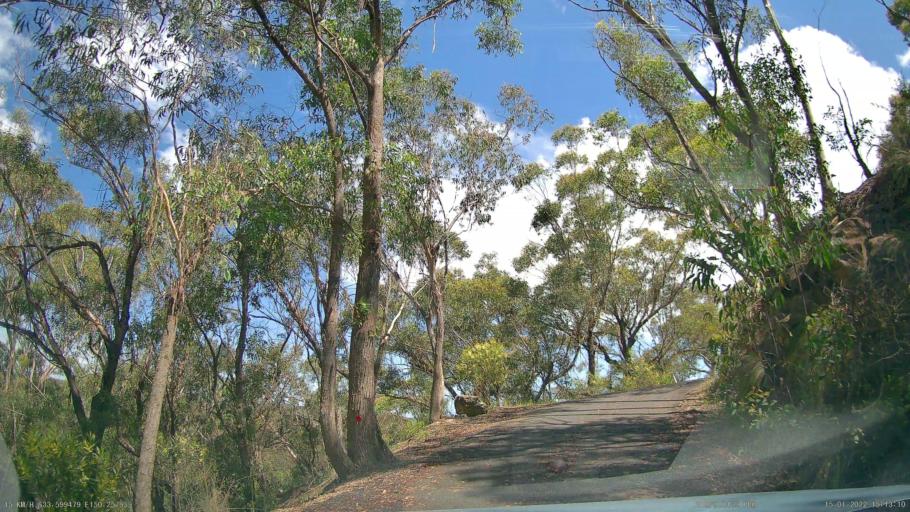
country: AU
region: New South Wales
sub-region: Blue Mountains Municipality
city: Blackheath
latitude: -33.5995
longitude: 150.2580
